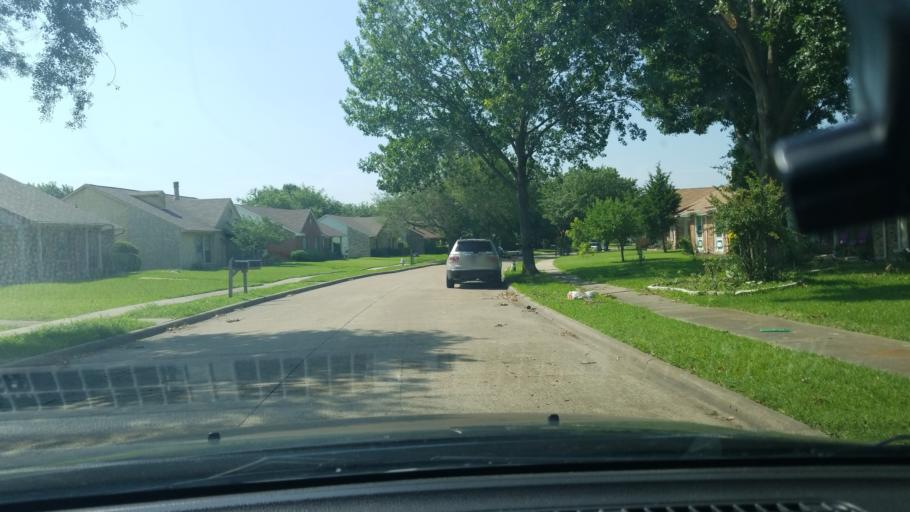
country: US
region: Texas
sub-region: Dallas County
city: Mesquite
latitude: 32.8218
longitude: -96.6248
